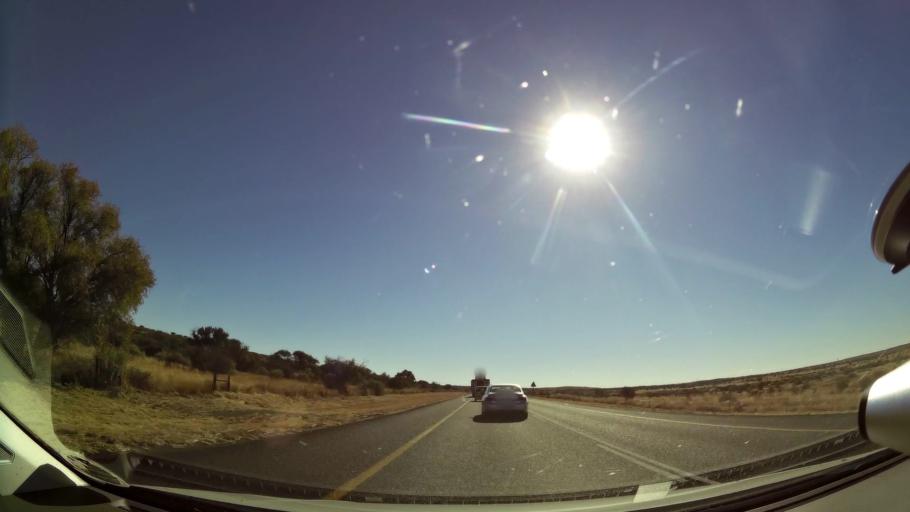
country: ZA
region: Northern Cape
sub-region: Frances Baard District Municipality
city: Warrenton
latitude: -28.3190
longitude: 24.8253
